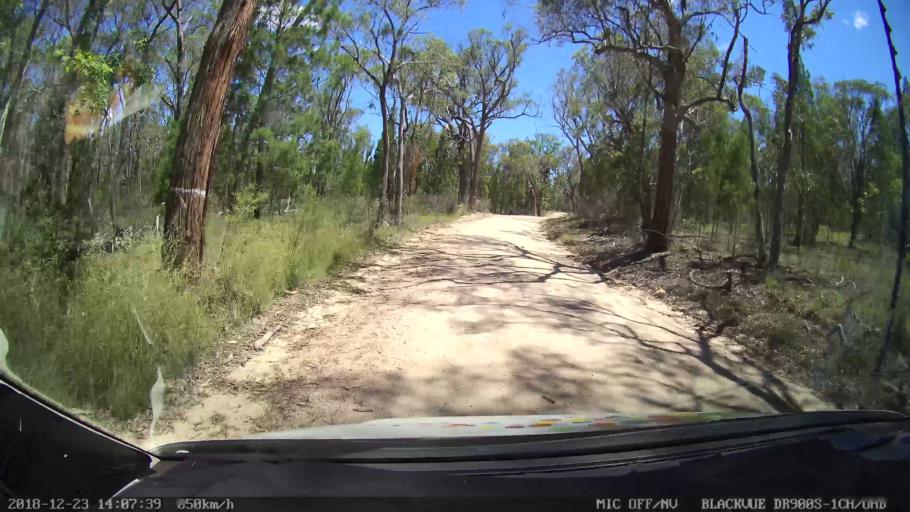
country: AU
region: New South Wales
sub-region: Tamworth Municipality
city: Manilla
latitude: -30.6374
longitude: 151.0713
